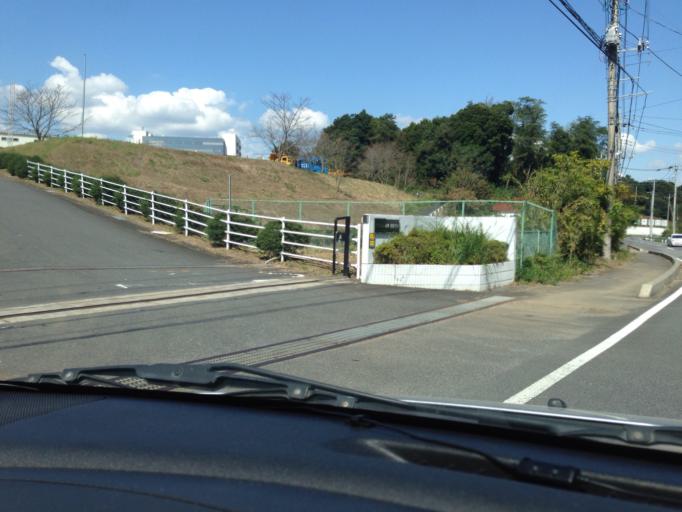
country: JP
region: Ibaraki
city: Inashiki
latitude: 36.0163
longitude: 140.3022
